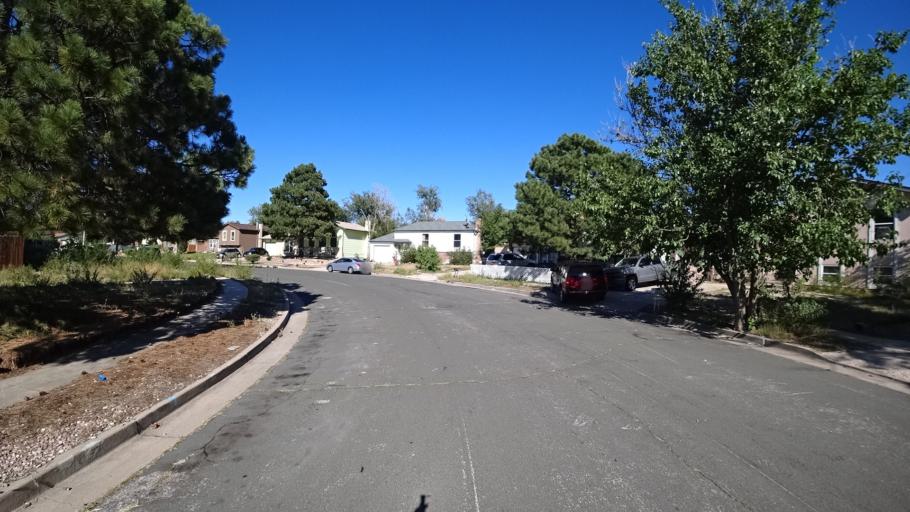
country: US
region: Colorado
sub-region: El Paso County
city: Stratmoor
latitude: 38.7958
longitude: -104.7523
